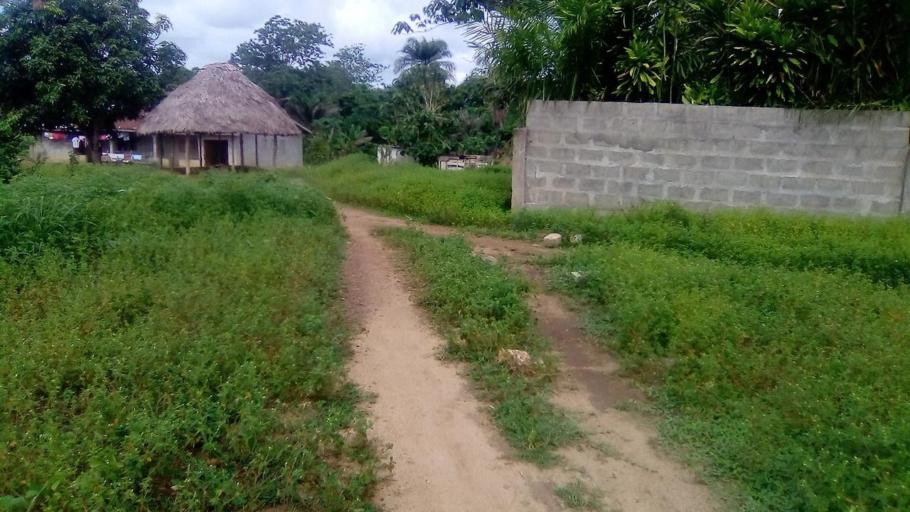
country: SL
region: Southern Province
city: Pujehun
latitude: 7.3691
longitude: -11.7276
